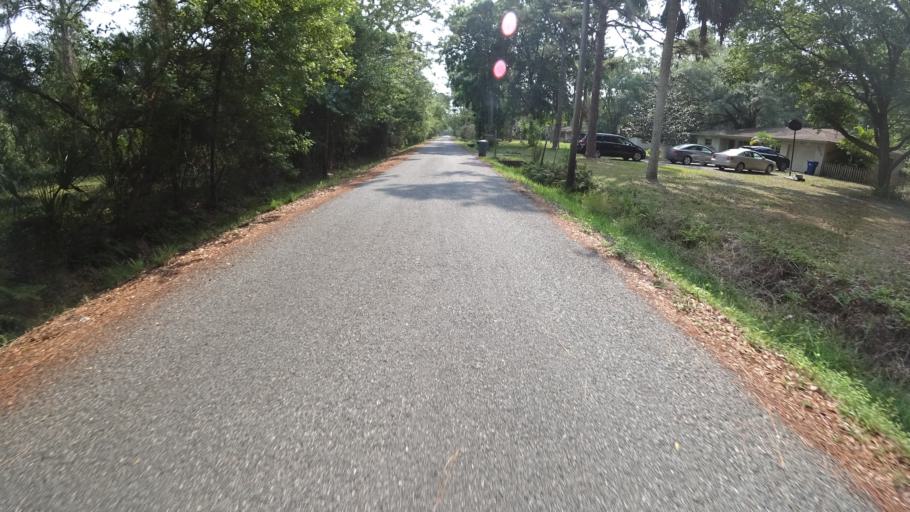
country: US
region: Florida
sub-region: Manatee County
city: Samoset
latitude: 27.4730
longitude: -82.5014
